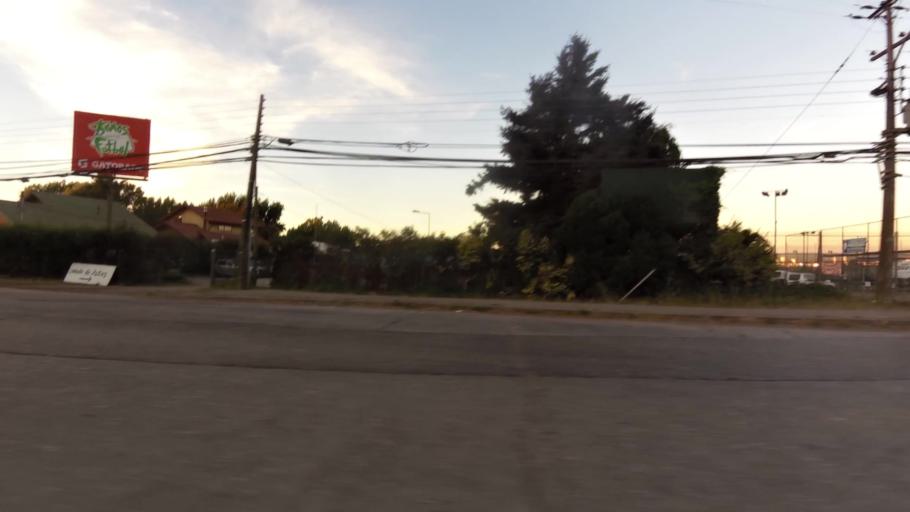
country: CL
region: Biobio
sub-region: Provincia de Concepcion
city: Concepcion
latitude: -36.8394
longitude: -73.0853
